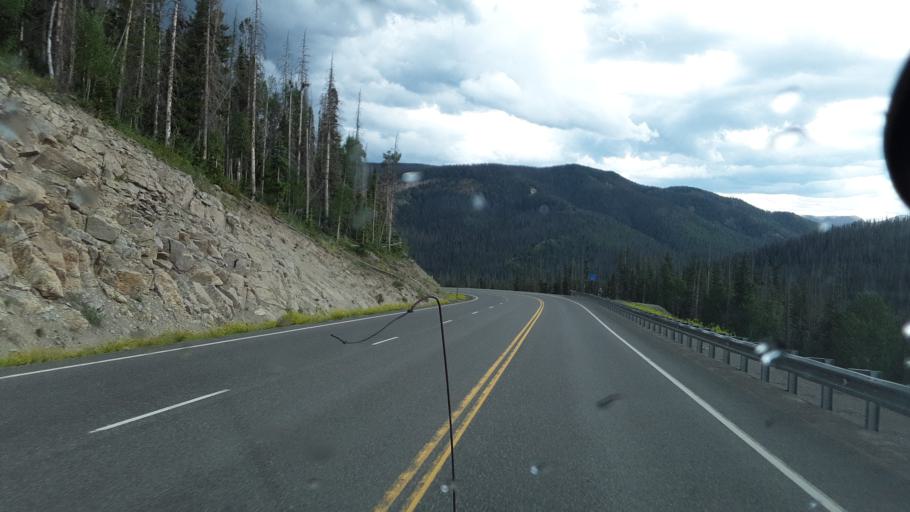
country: US
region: Colorado
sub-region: Archuleta County
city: Pagosa Springs
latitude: 37.4796
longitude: -106.7736
